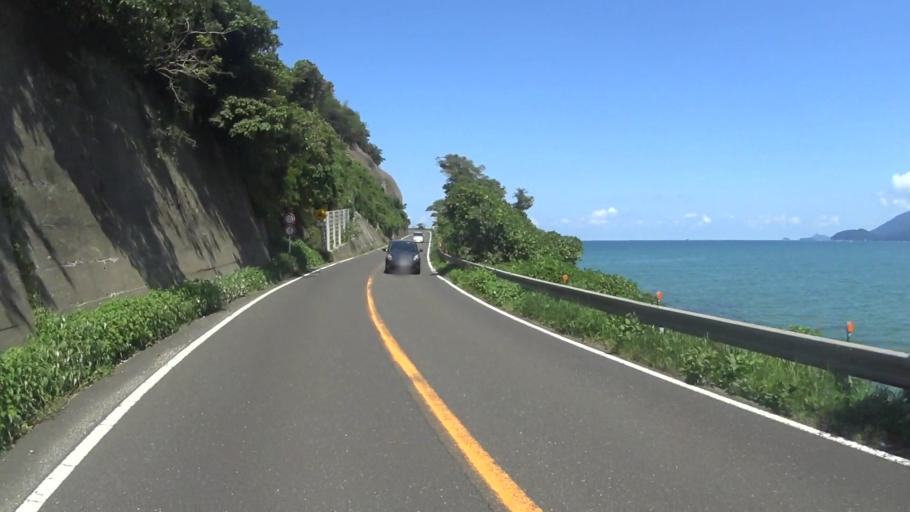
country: JP
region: Kyoto
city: Miyazu
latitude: 35.5254
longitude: 135.2714
